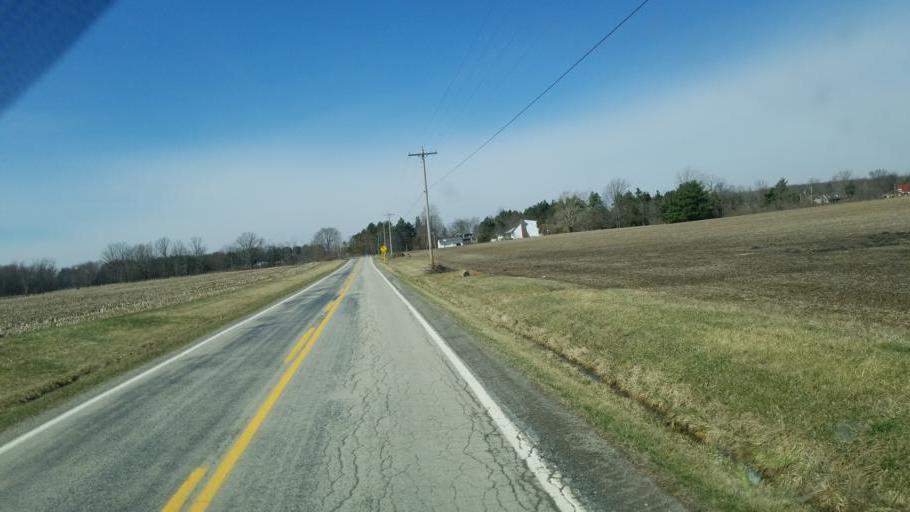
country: US
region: Ohio
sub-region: Lorain County
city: Wellington
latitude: 41.1291
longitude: -82.2653
